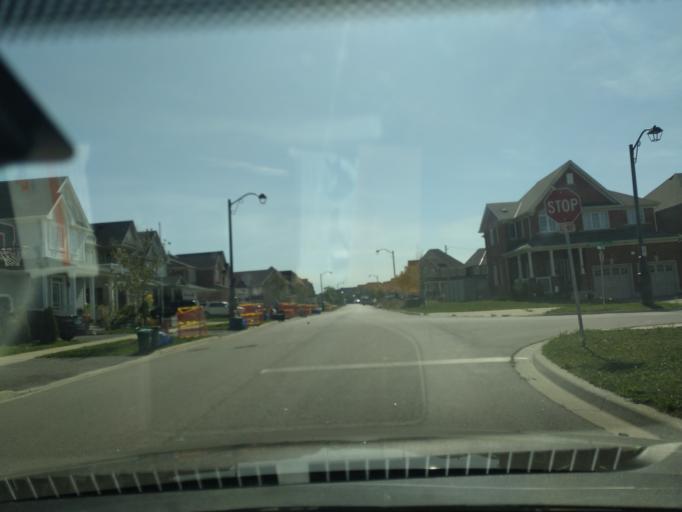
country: CA
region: Ontario
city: Keswick
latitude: 44.2026
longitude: -79.4628
